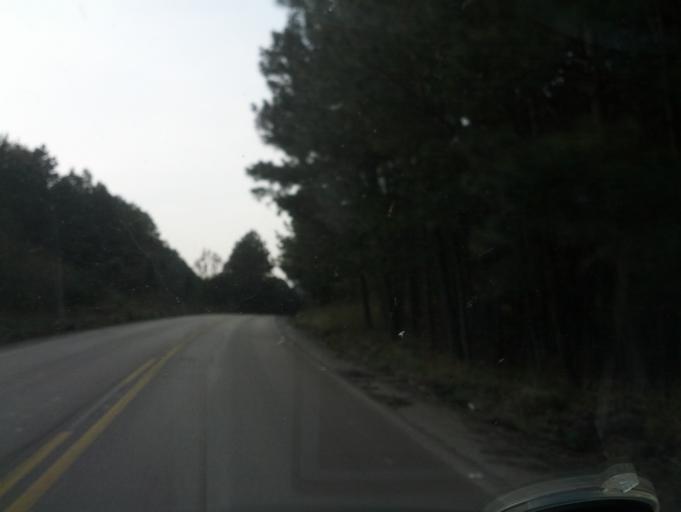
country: BR
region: Santa Catarina
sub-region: Otacilio Costa
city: Otacilio Costa
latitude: -27.3172
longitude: -50.1369
